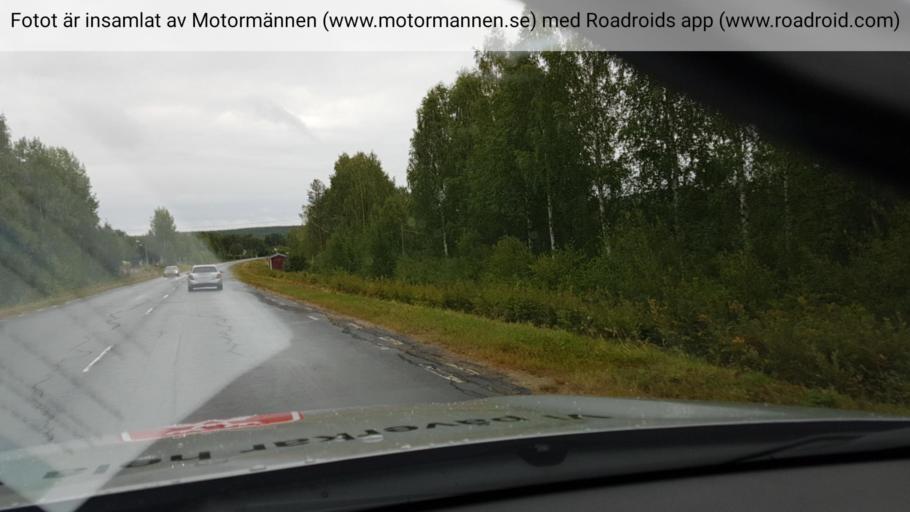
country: SE
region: Norrbotten
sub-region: Alvsbyns Kommun
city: AElvsbyn
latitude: 66.0869
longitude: 20.9045
